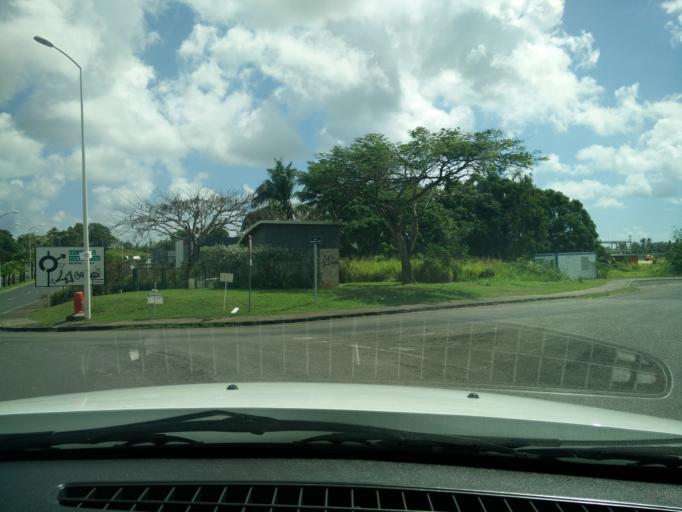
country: GP
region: Guadeloupe
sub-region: Guadeloupe
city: Les Abymes
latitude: 16.2699
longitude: -61.5176
